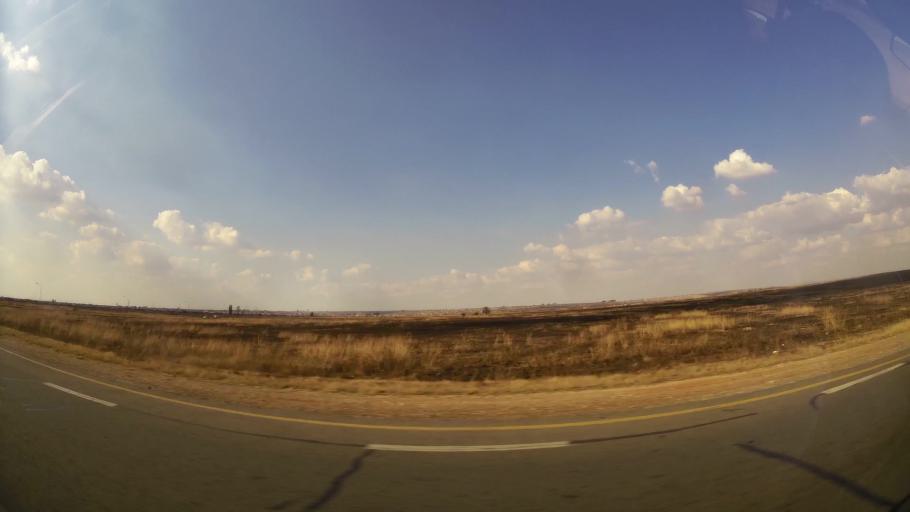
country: ZA
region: Gauteng
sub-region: Sedibeng District Municipality
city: Heidelberg
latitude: -26.3832
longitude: 28.3446
